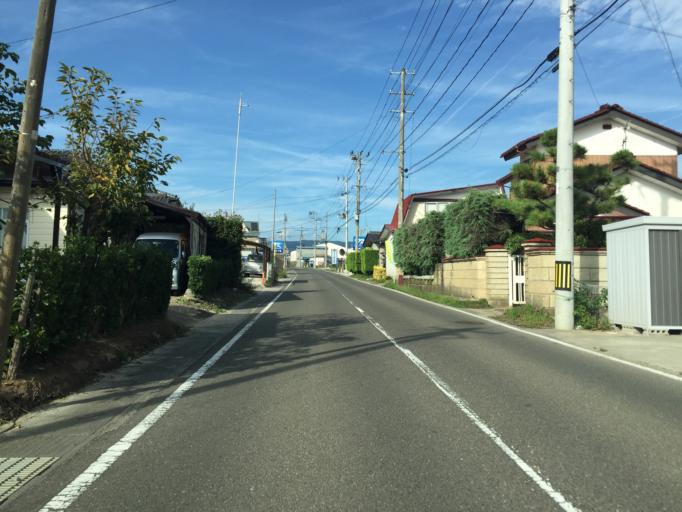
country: JP
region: Fukushima
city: Hobaramachi
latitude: 37.8388
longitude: 140.5115
